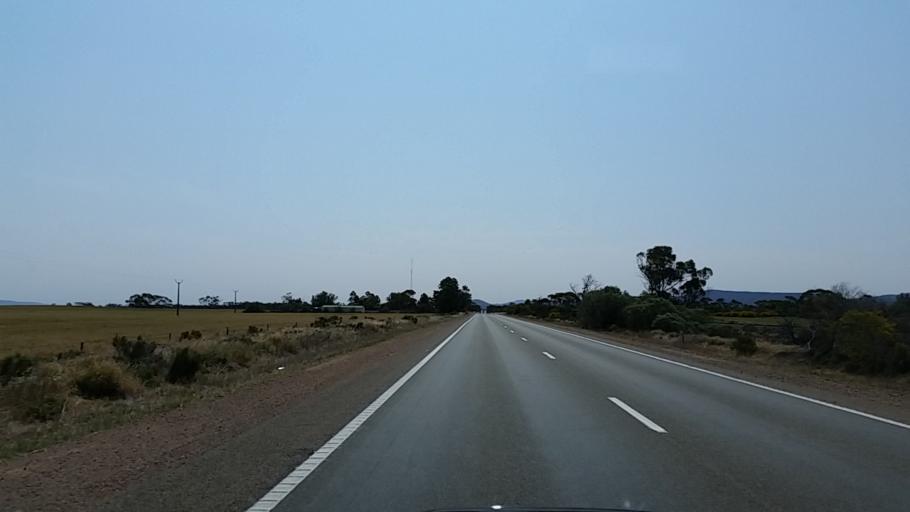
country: AU
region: South Australia
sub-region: Port Pirie City and Dists
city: Port Pirie
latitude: -32.9286
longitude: 137.9824
